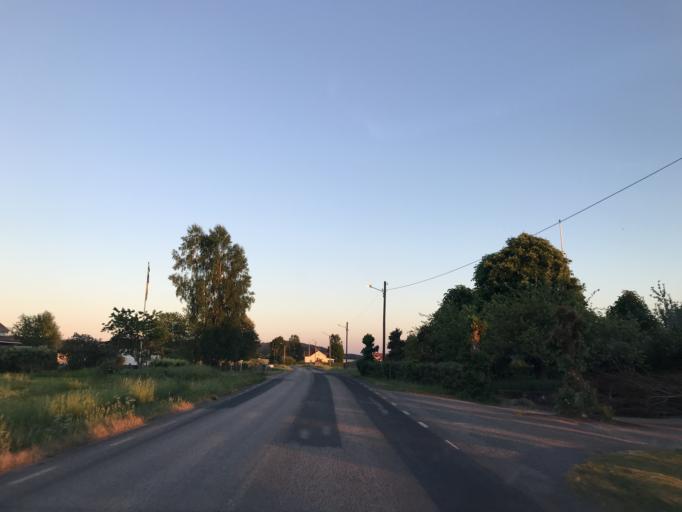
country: SE
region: Vaestra Goetaland
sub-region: Marks Kommun
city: Horred
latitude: 57.4339
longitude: 12.5166
